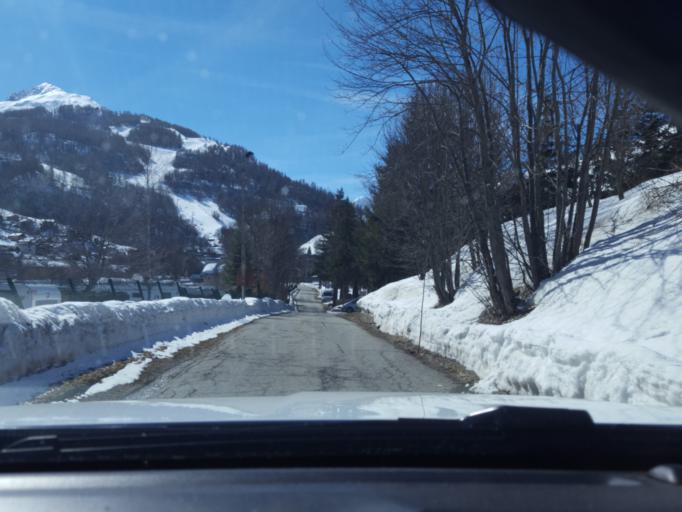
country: FR
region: Rhone-Alpes
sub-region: Departement de la Savoie
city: Valloire
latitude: 45.1710
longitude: 6.4296
